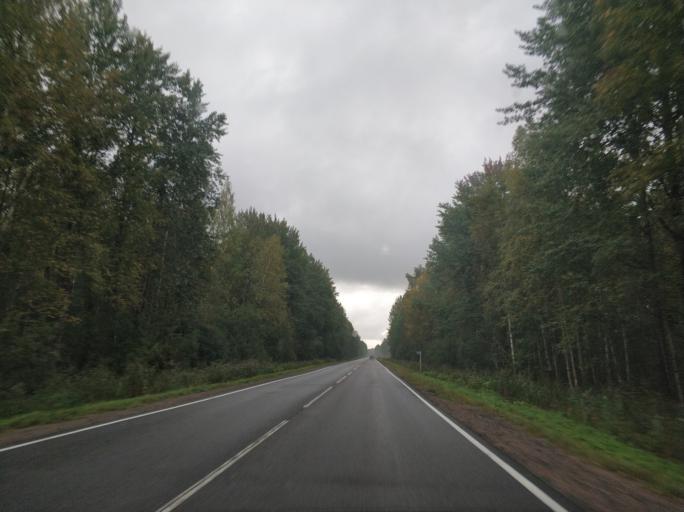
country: RU
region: Leningrad
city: Borisova Griva
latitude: 60.1199
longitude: 30.9636
